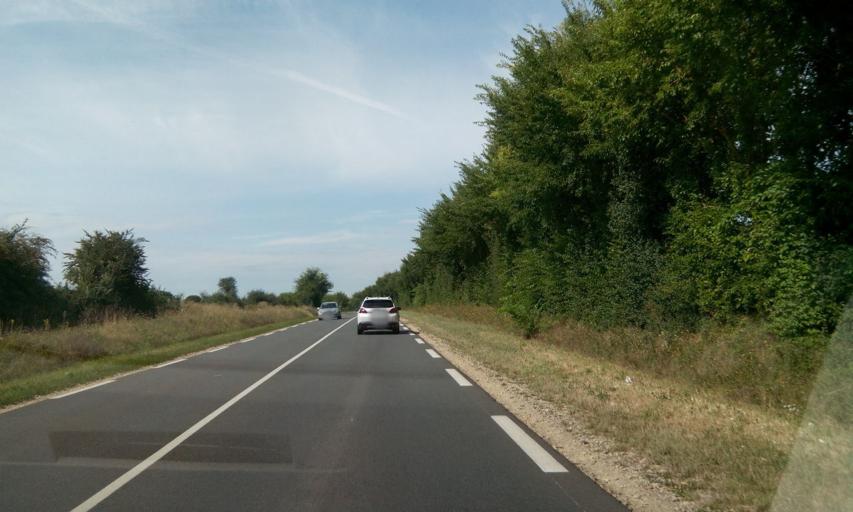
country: FR
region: Poitou-Charentes
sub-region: Departement de la Vienne
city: Civray
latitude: 46.1565
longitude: 0.2857
